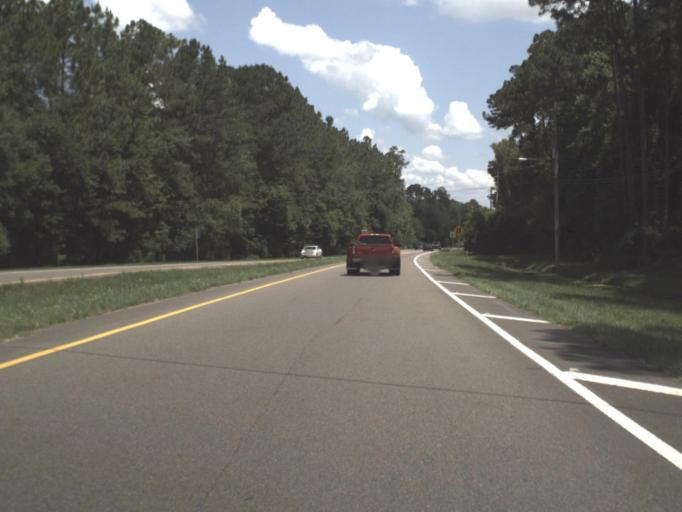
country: US
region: Florida
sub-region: Nassau County
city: Nassau Village-Ratliff
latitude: 30.4586
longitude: -81.7065
